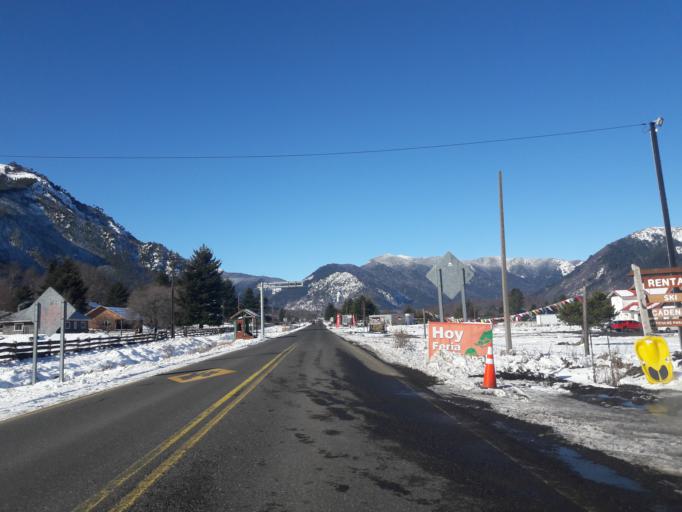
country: CL
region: Araucania
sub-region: Provincia de Cautin
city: Vilcun
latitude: -38.4713
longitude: -71.5750
